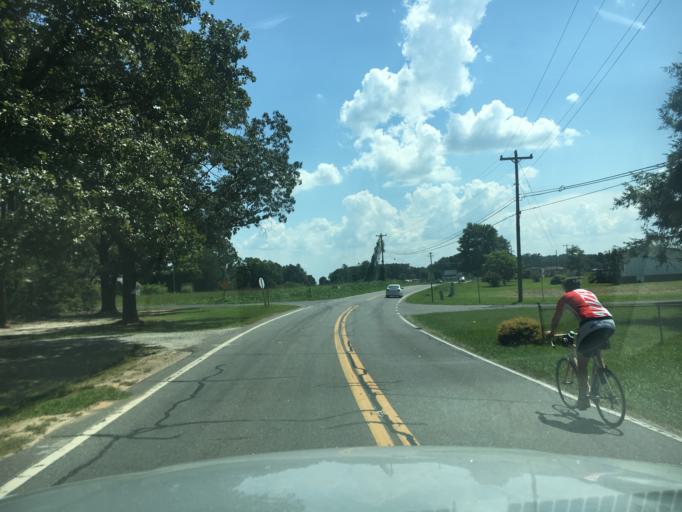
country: US
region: North Carolina
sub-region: Rutherford County
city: Forest City
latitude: 35.2854
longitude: -81.8410
